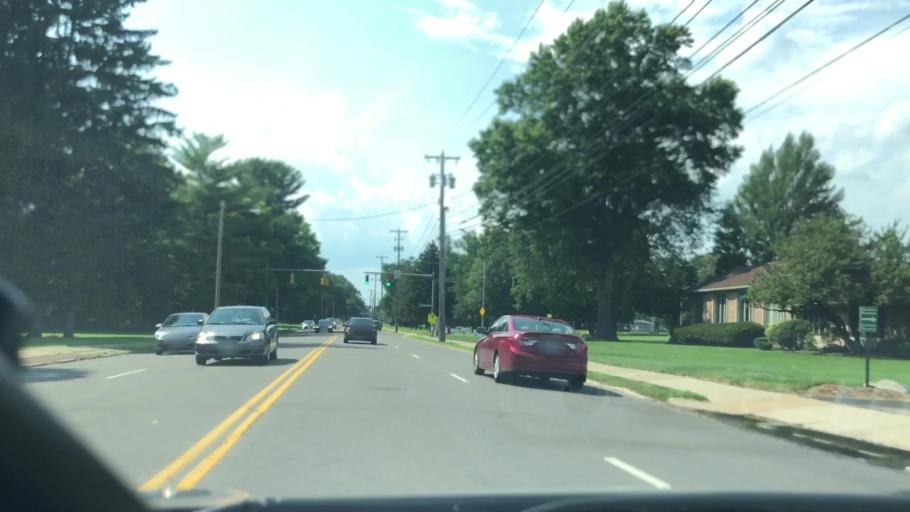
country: US
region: Ohio
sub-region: Summit County
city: Fairlawn
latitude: 41.1151
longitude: -81.5820
